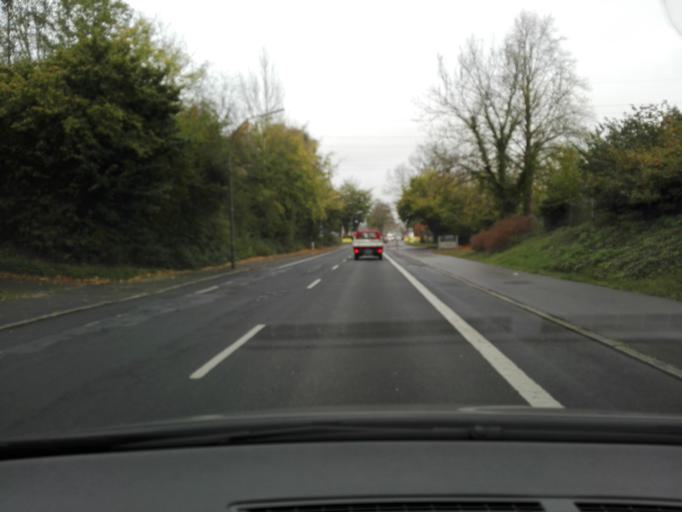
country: DE
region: North Rhine-Westphalia
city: Lanstrop
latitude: 51.5173
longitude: 7.5367
